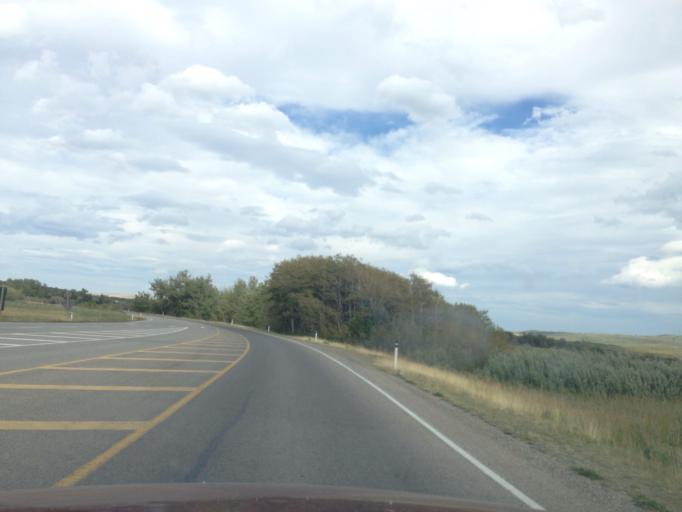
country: CA
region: Alberta
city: Pincher Creek
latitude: 49.1097
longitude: -113.8486
